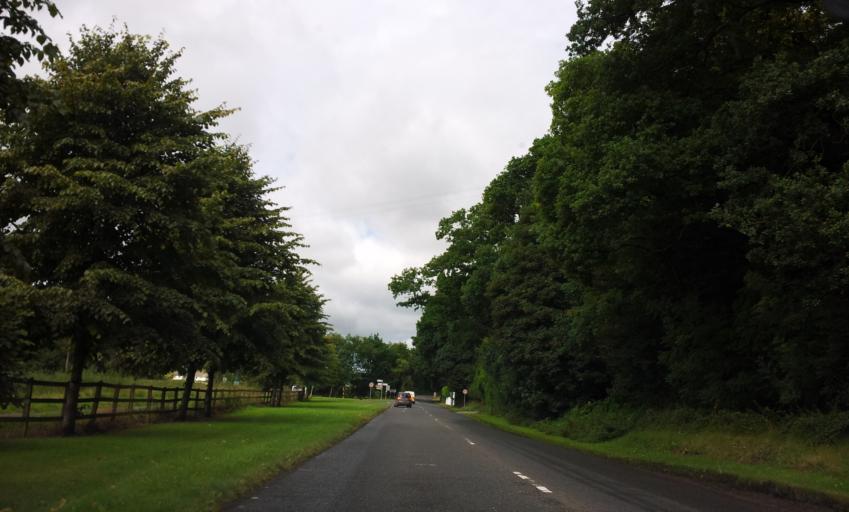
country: IE
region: Munster
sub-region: County Cork
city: Blarney
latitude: 51.9312
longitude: -8.5510
